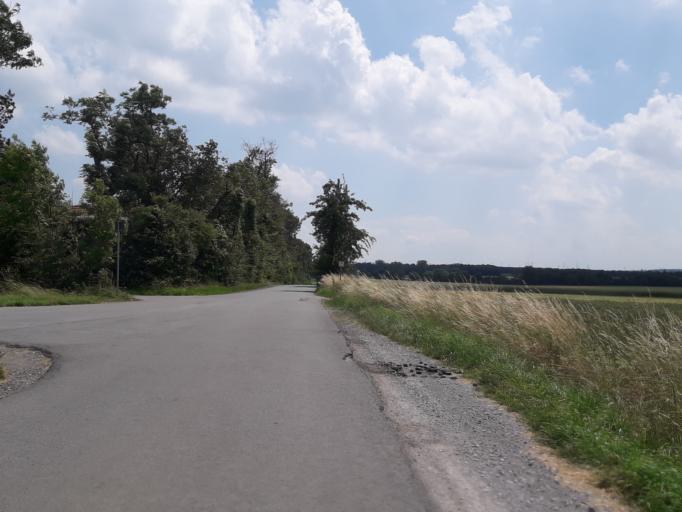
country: DE
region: North Rhine-Westphalia
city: Bad Lippspringe
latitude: 51.7397
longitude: 8.7976
